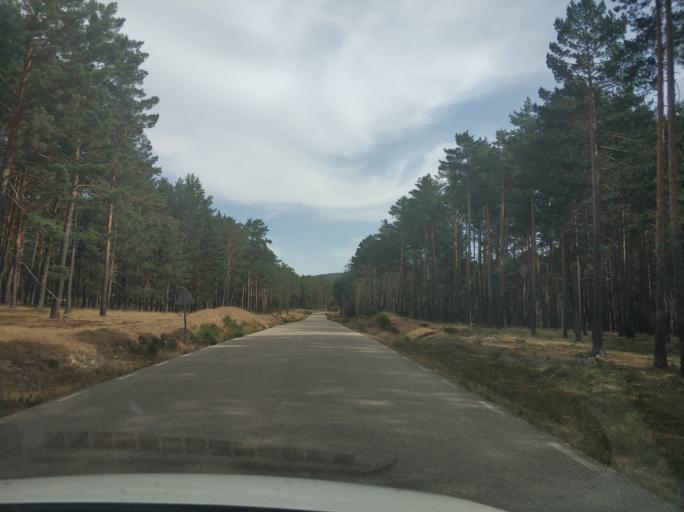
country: ES
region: Castille and Leon
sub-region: Provincia de Soria
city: Navaleno
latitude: 41.8686
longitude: -2.9445
